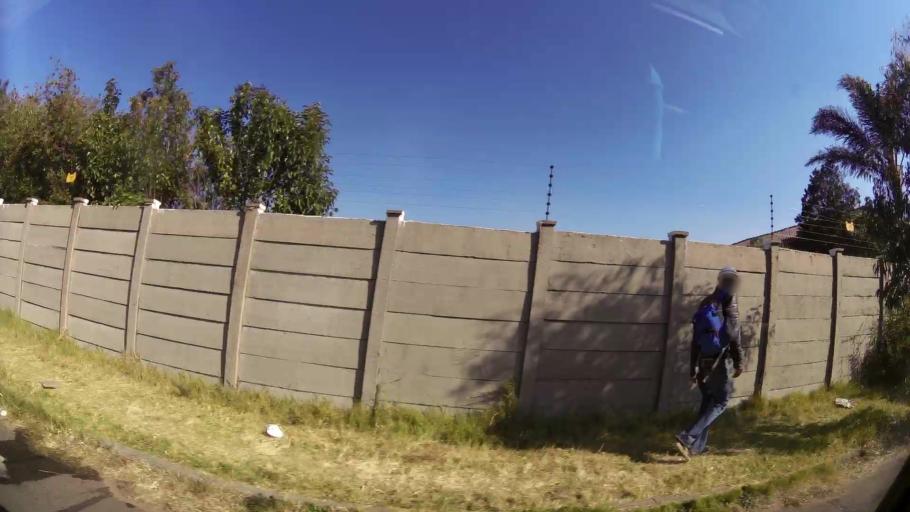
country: ZA
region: Gauteng
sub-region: City of Johannesburg Metropolitan Municipality
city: Johannesburg
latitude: -26.2582
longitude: 28.0154
